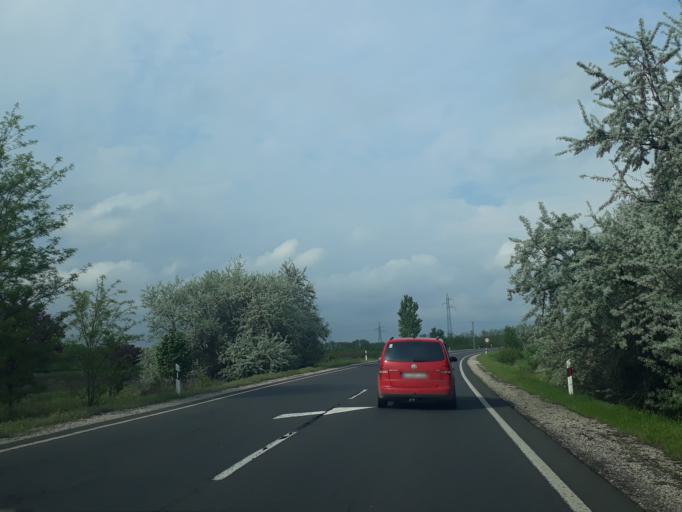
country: HU
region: Szabolcs-Szatmar-Bereg
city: Nyirbogdany
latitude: 48.0638
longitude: 21.9293
